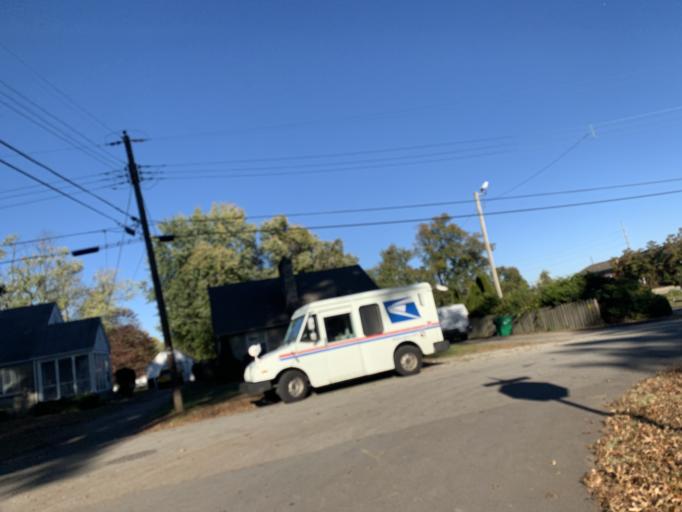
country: US
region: Kentucky
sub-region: Jefferson County
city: Saint Dennis
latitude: 38.1735
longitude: -85.8261
